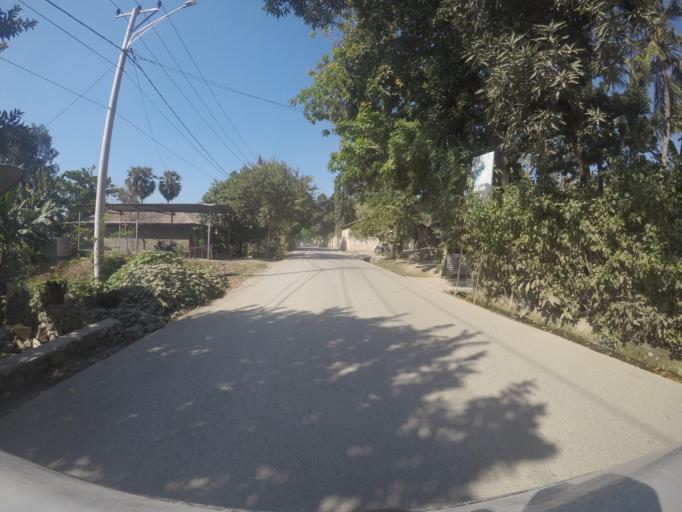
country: TL
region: Dili
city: Dili
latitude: -8.5754
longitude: 125.5411
